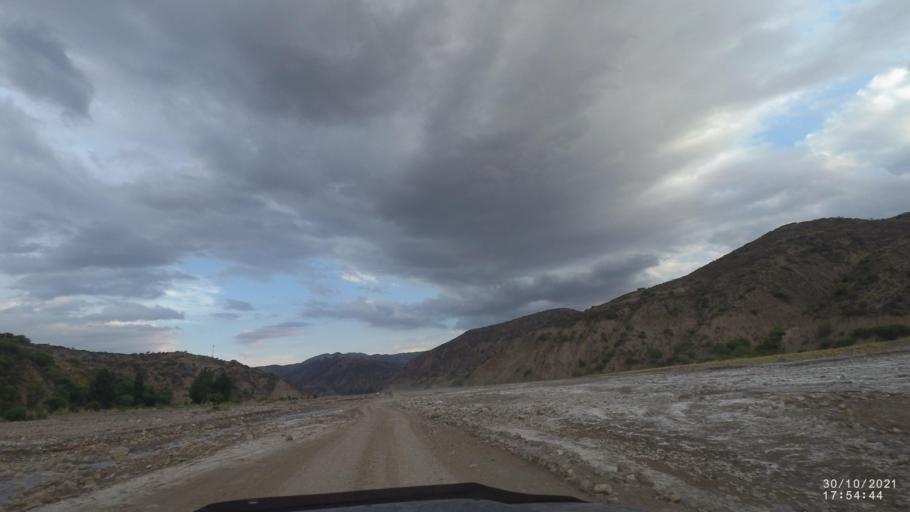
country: BO
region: Cochabamba
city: Sipe Sipe
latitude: -17.5434
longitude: -66.4880
